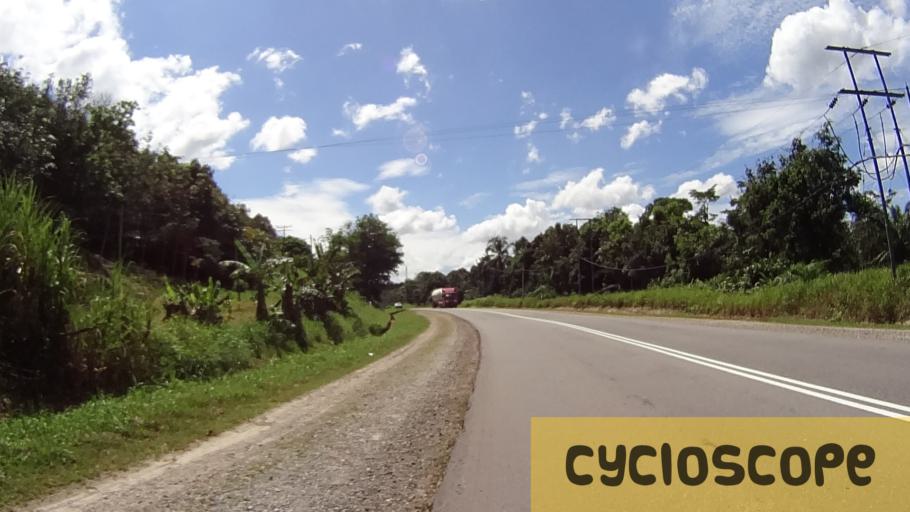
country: MY
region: Sabah
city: Beaufort
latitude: 5.2123
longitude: 115.6354
